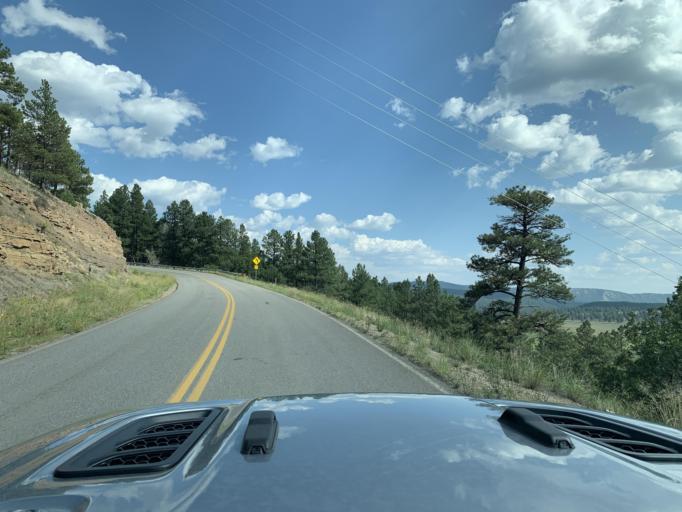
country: US
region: Colorado
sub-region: Archuleta County
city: Pagosa Springs
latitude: 37.2408
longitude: -107.0270
